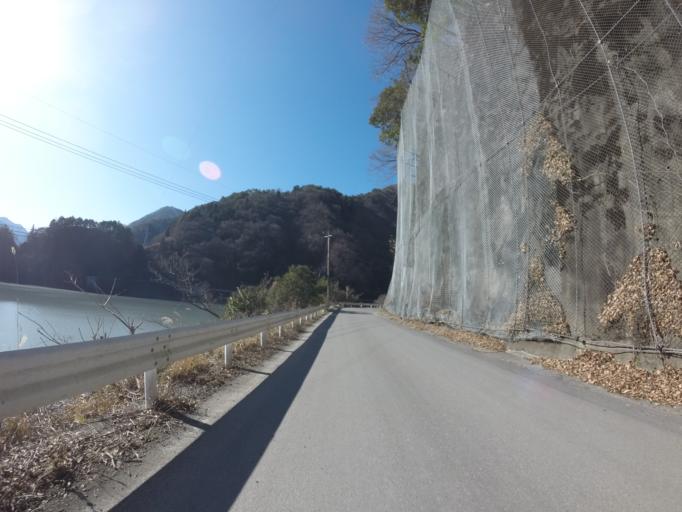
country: JP
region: Yamanashi
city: Ryuo
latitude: 35.4094
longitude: 138.3318
